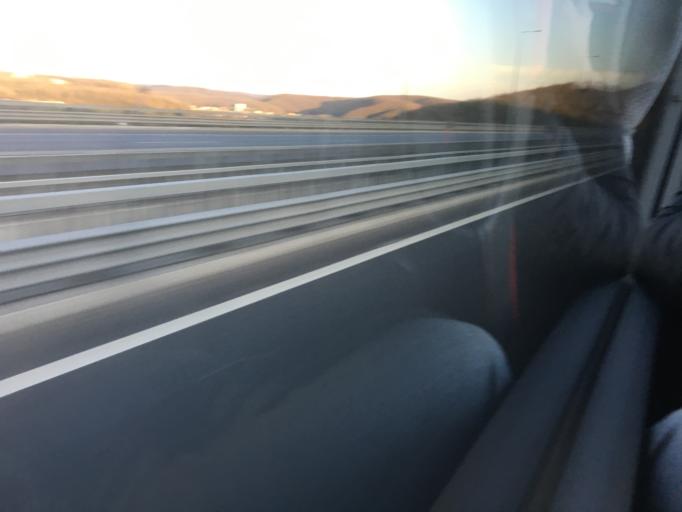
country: TR
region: Istanbul
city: Mahmut Sevket Pasa
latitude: 41.1406
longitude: 29.2845
